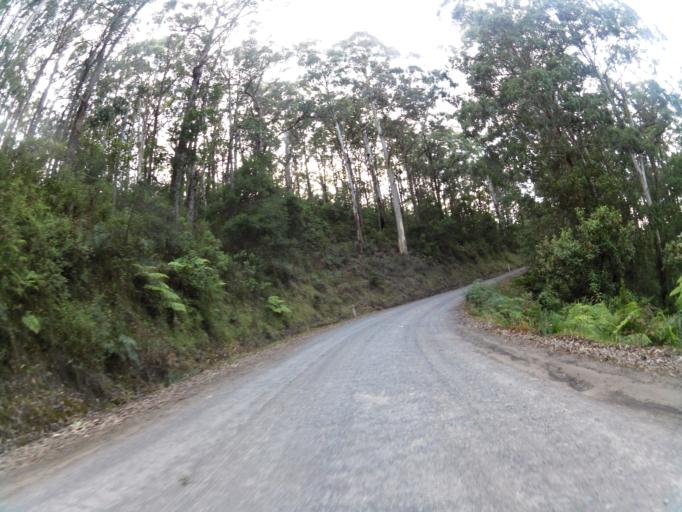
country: AU
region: Victoria
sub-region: Colac-Otway
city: Apollo Bay
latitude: -38.5508
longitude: 143.7366
